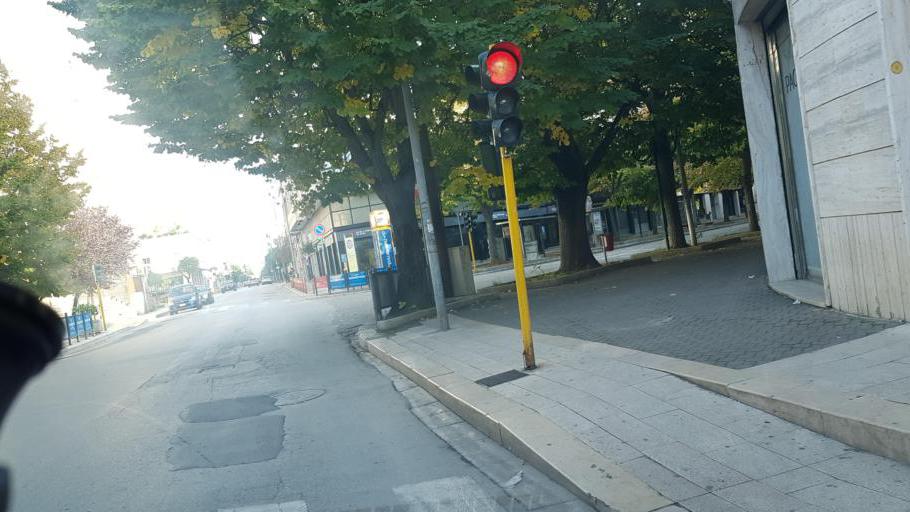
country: IT
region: Apulia
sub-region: Provincia di Brindisi
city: Francavilla Fontana
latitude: 40.5272
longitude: 17.5831
